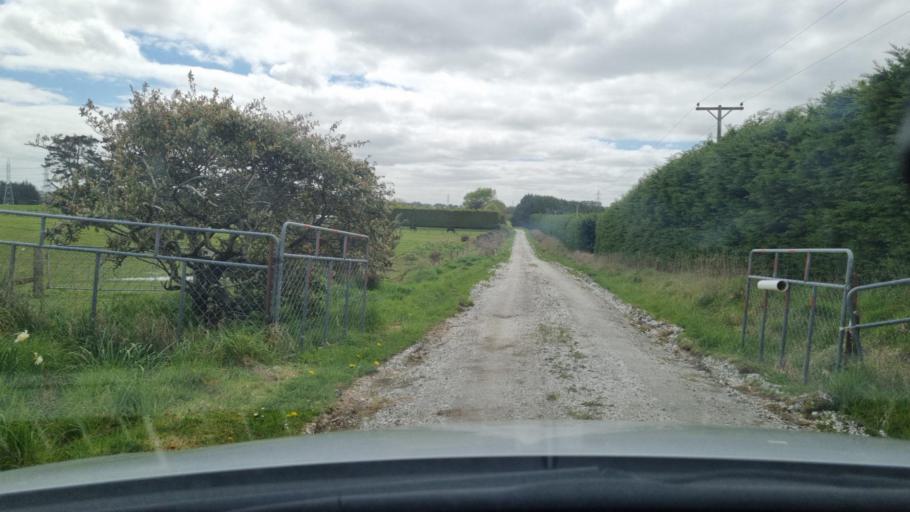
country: NZ
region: Southland
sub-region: Invercargill City
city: Invercargill
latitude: -46.3912
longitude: 168.4052
